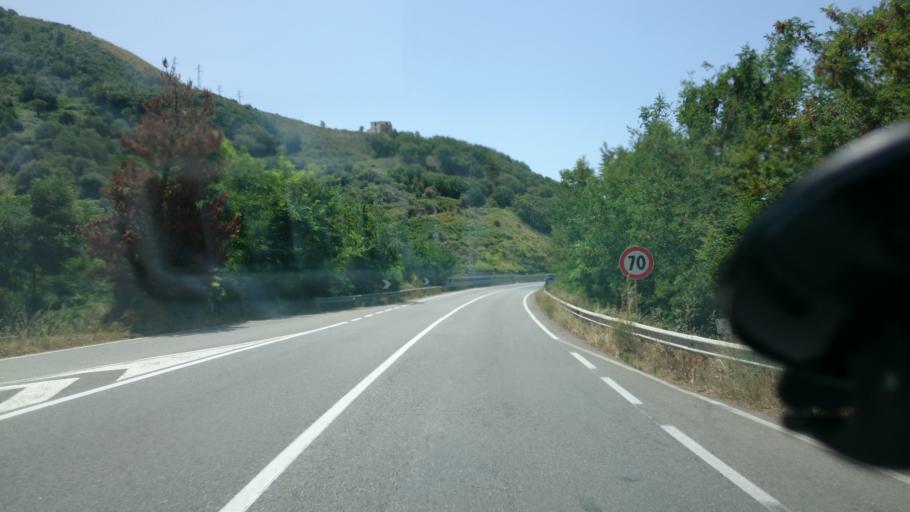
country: IT
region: Calabria
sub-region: Provincia di Cosenza
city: Cittadella del Capo
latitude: 39.5880
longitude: 15.8698
